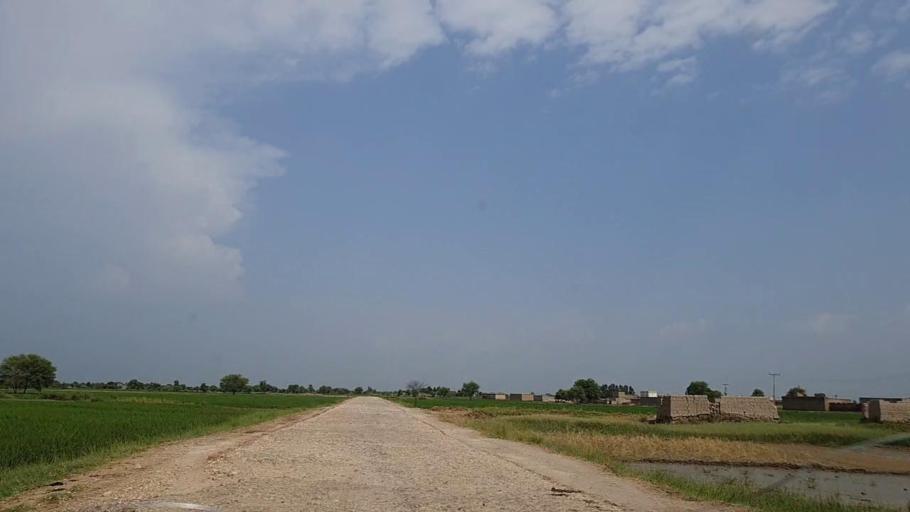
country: PK
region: Sindh
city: Khanpur
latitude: 27.8478
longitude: 69.4487
